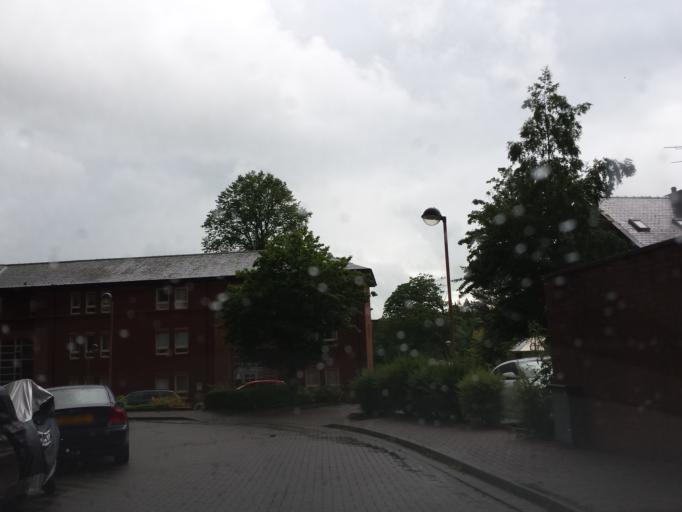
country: GB
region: Scotland
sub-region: Dumfries and Galloway
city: Dumfries
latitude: 55.0637
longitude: -3.6060
